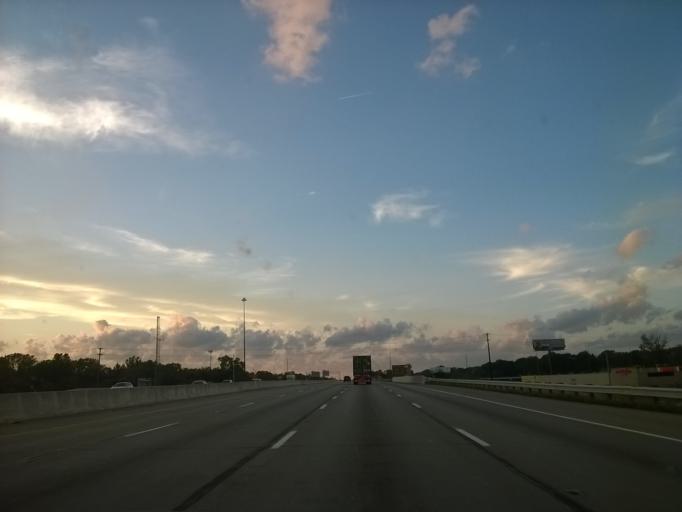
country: US
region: Indiana
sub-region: Marion County
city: Lawrence
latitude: 39.8311
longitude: -86.0349
